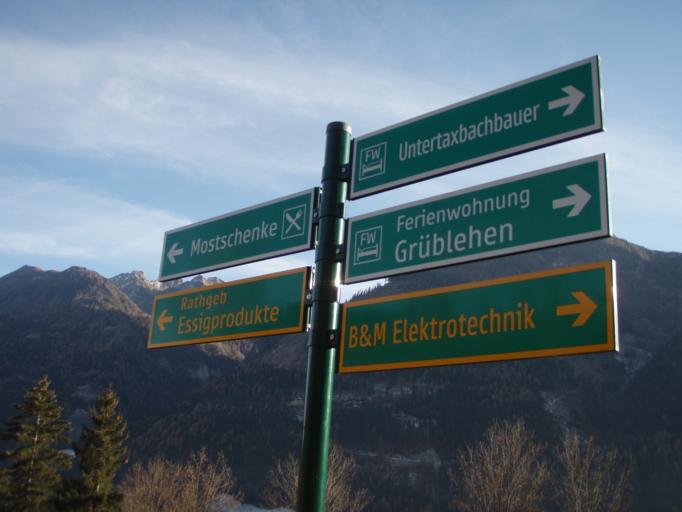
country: AT
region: Salzburg
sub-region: Politischer Bezirk Sankt Johann im Pongau
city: Goldegg
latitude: 47.3108
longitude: 13.1017
